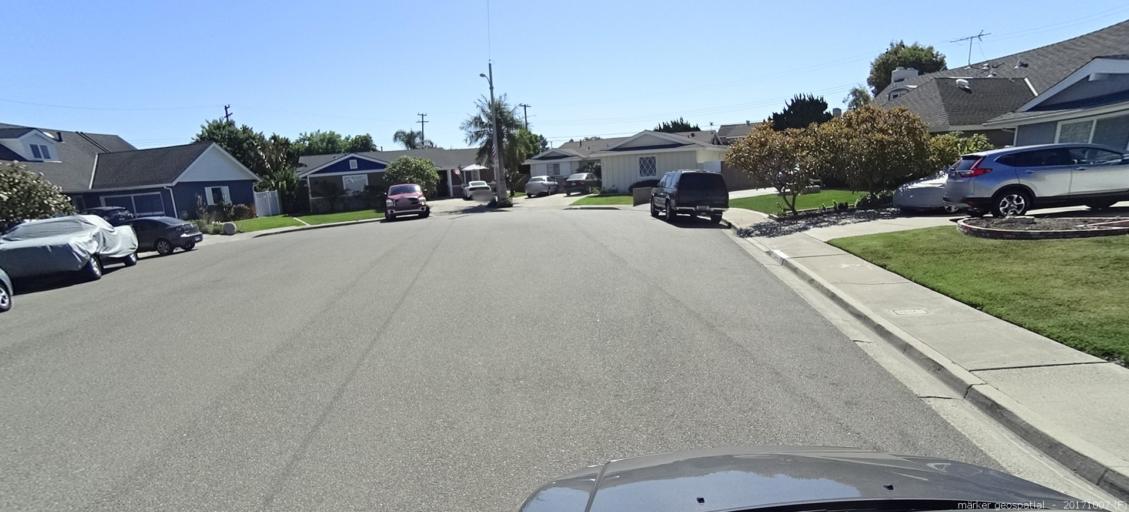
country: US
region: California
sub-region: Orange County
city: Westminster
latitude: 33.7819
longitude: -118.0334
